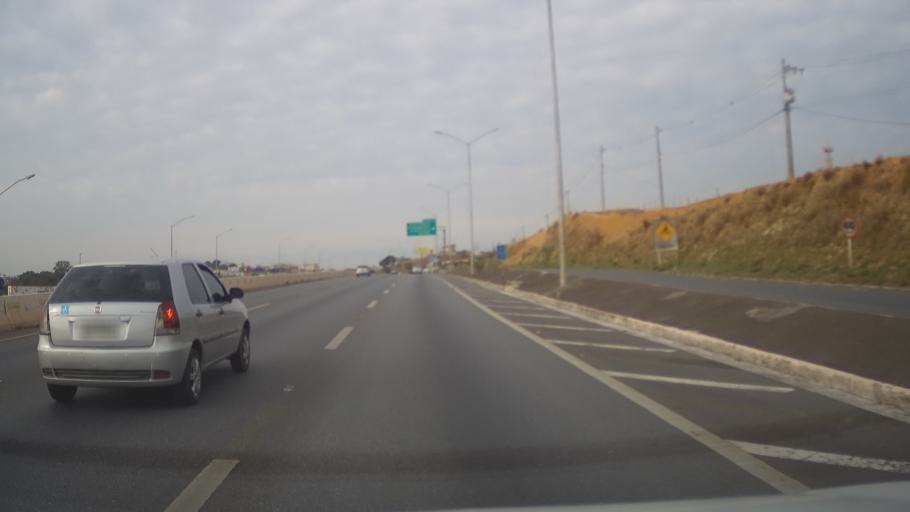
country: BR
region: Minas Gerais
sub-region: Vespasiano
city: Vespasiano
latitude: -19.7401
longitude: -43.9488
